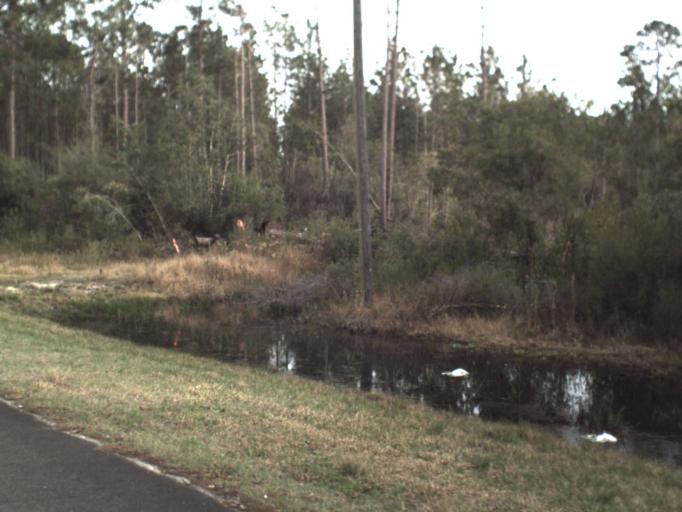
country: US
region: Florida
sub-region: Gulf County
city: Wewahitchka
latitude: 30.1362
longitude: -85.3735
